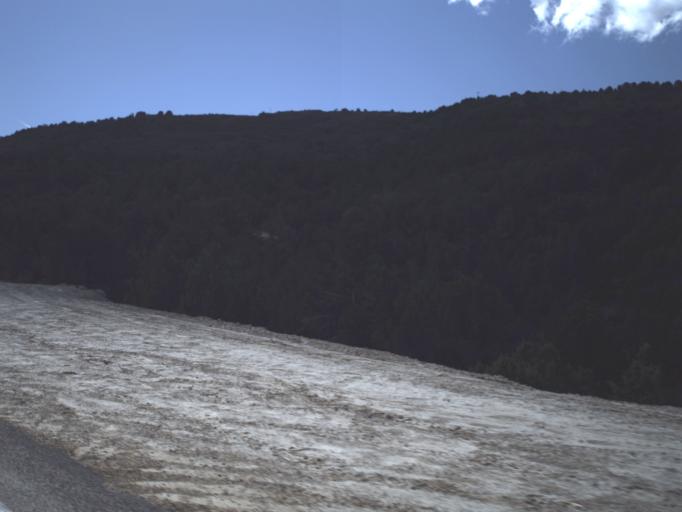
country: US
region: Utah
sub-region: Washington County
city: Enterprise
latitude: 37.5302
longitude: -113.6482
